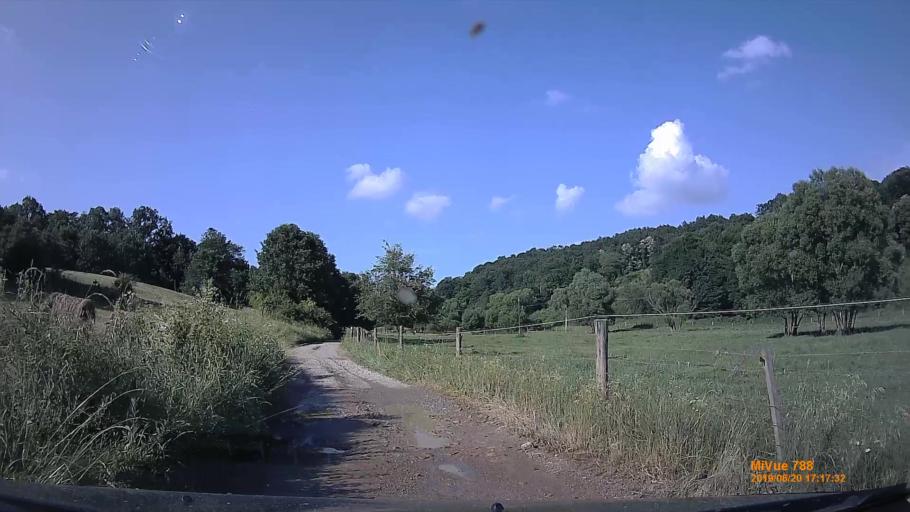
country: HU
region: Baranya
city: Buekkoesd
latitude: 46.1573
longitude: 18.0102
